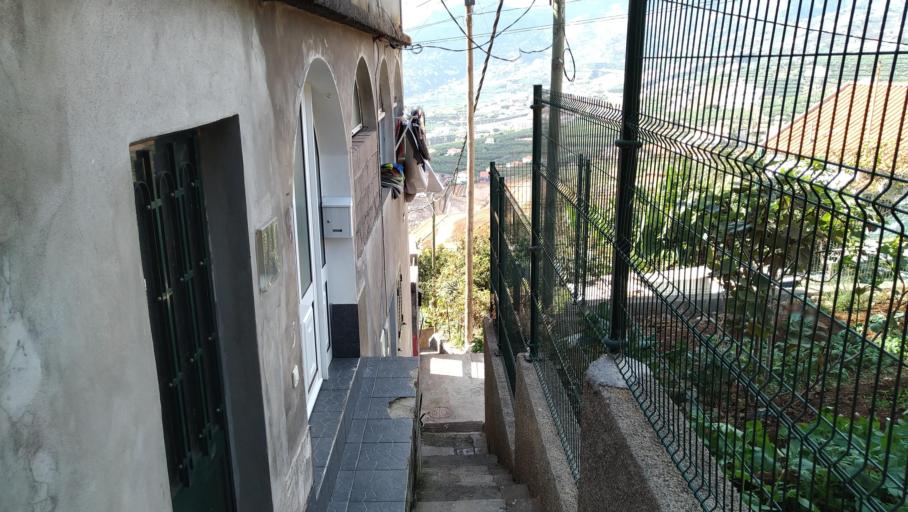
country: PT
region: Madeira
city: Camara de Lobos
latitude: 32.6529
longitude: -16.9503
